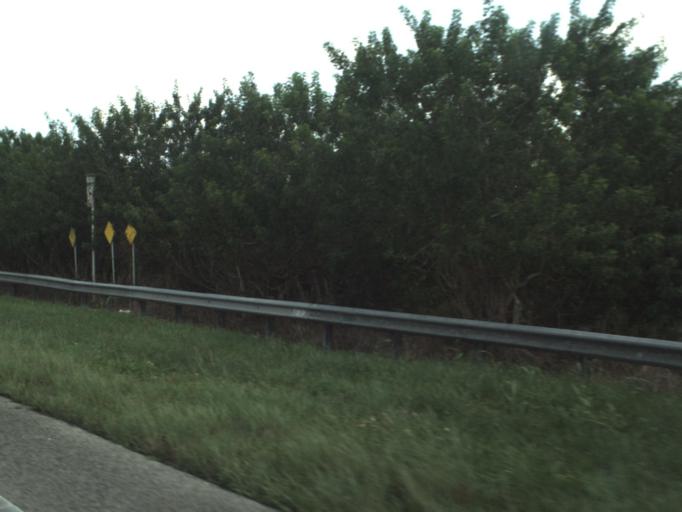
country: US
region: Florida
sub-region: Broward County
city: Weston
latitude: 26.2344
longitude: -80.4613
